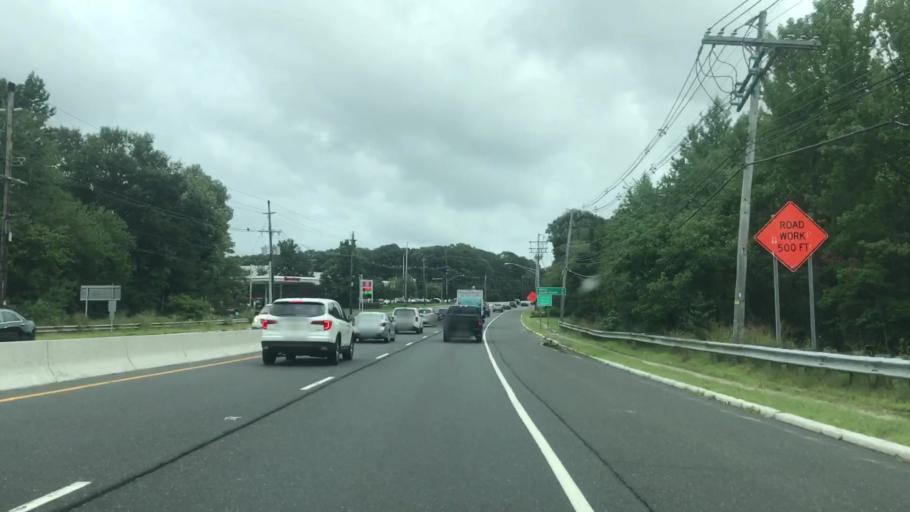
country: US
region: New Jersey
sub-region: Monmouth County
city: Eatontown
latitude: 40.2739
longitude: -74.0438
